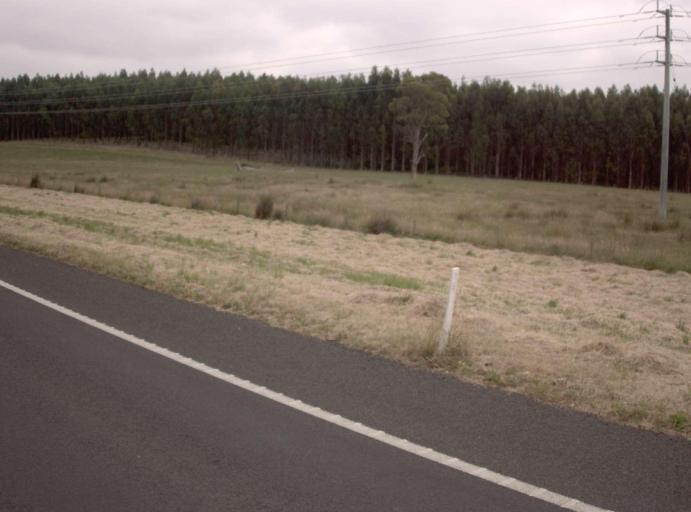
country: AU
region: Victoria
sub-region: Latrobe
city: Morwell
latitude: -38.2391
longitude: 146.3423
